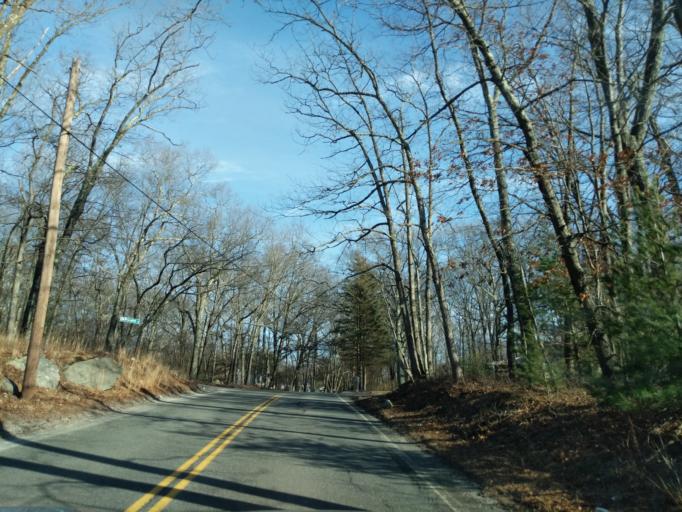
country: US
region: Massachusetts
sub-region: Worcester County
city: Millville
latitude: 42.0265
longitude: -71.5637
